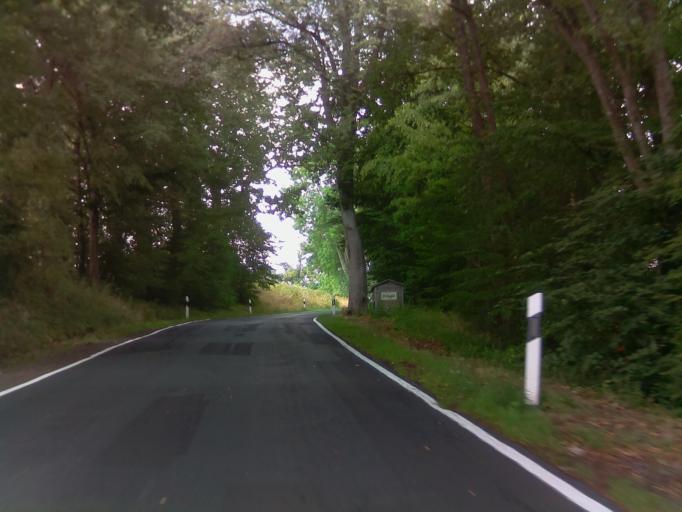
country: DE
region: Hesse
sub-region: Regierungsbezirk Kassel
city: Hosenfeld
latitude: 50.5679
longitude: 9.4420
